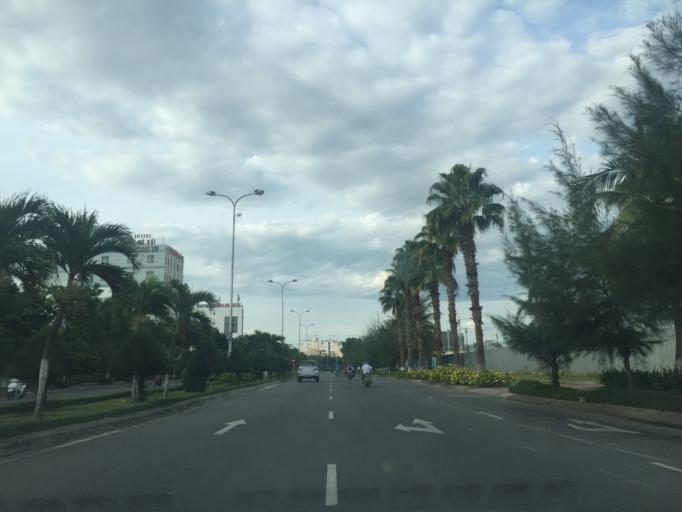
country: VN
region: Da Nang
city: Da Nang
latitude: 16.0856
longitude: 108.2141
